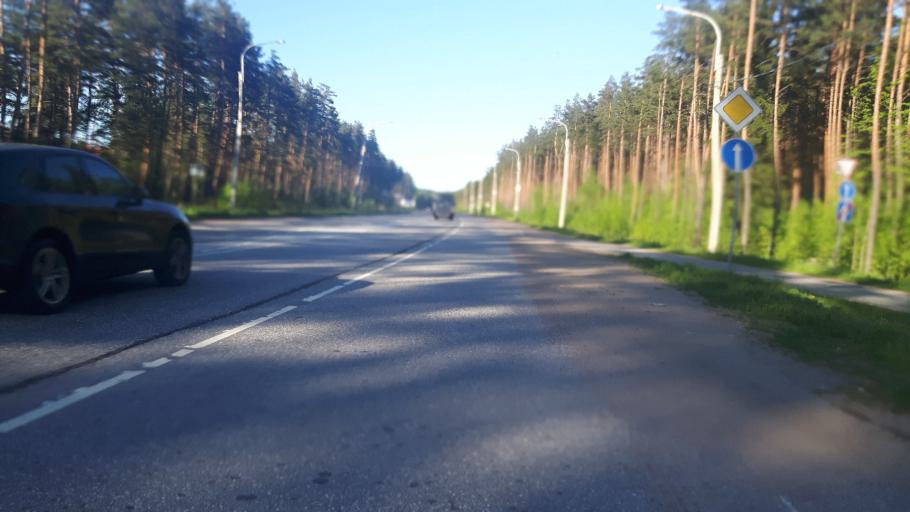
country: RU
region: Leningrad
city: Molodezhnoye
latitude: 60.1702
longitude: 29.4287
